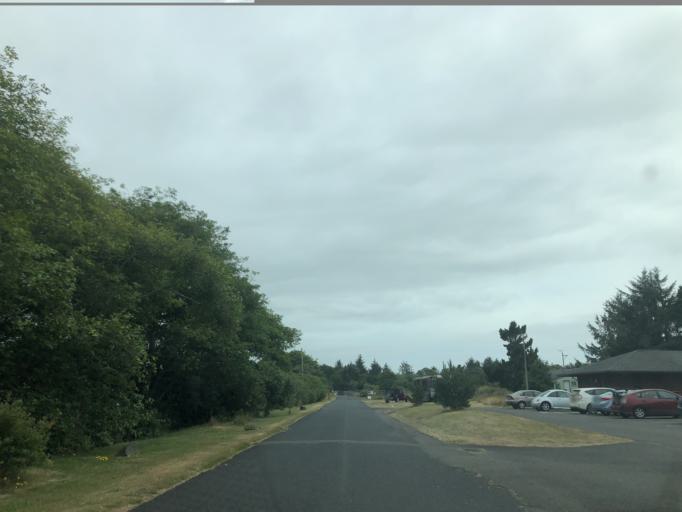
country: US
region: Oregon
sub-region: Lincoln County
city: Newport
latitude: 44.6204
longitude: -124.0458
